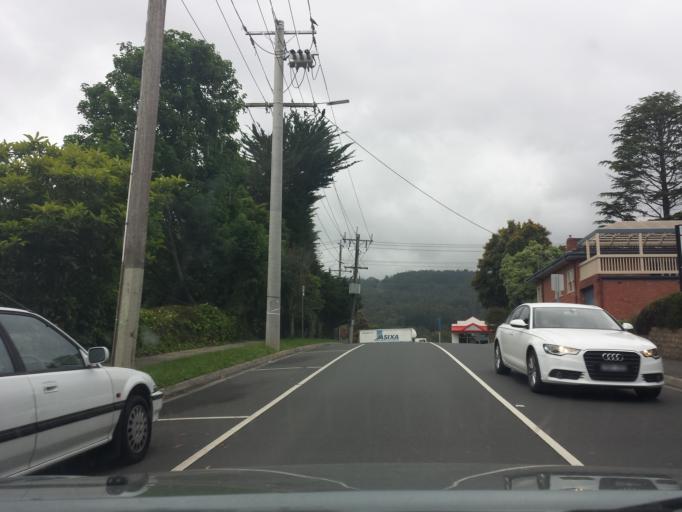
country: AU
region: Victoria
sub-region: Yarra Ranges
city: Tecoma
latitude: -37.9073
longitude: 145.3435
